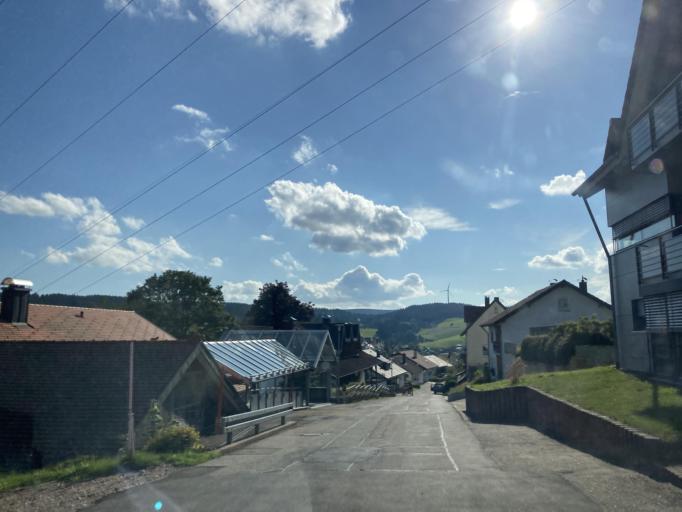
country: DE
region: Baden-Wuerttemberg
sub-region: Freiburg Region
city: Schonach im Schwarzwald
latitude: 48.1447
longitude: 8.2082
